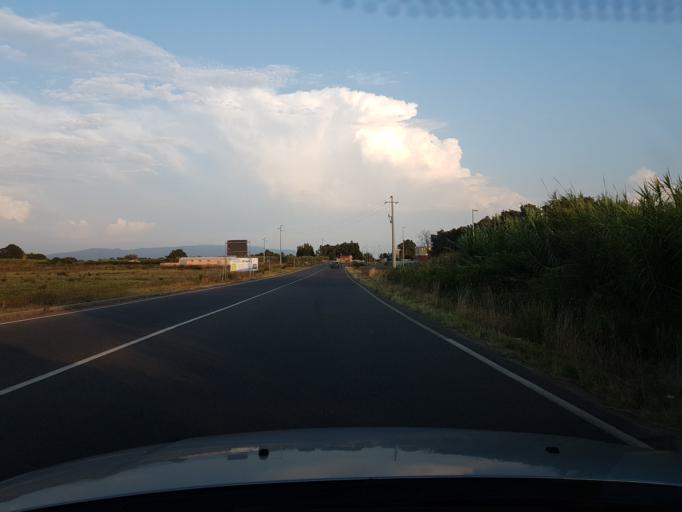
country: IT
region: Sardinia
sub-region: Provincia di Oristano
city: Cabras
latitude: 39.9187
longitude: 8.5382
